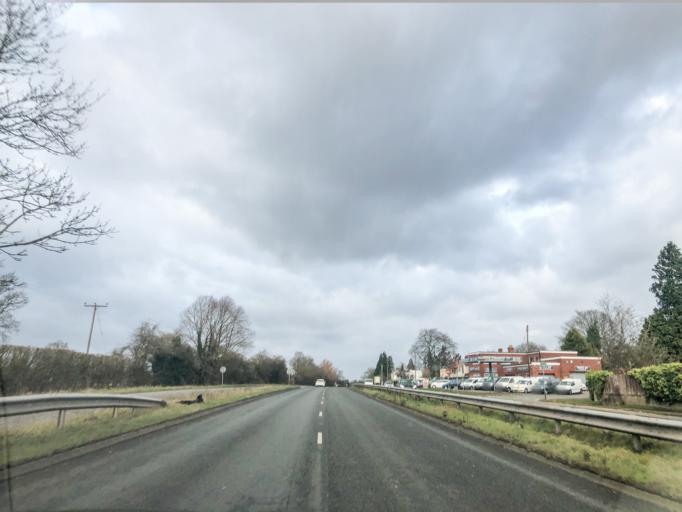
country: GB
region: England
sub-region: Solihull
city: Tidbury Green
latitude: 52.3634
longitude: -1.8894
